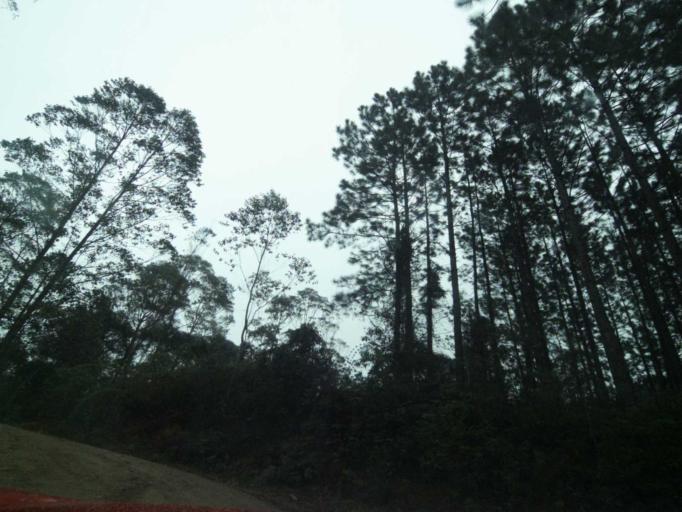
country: BR
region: Santa Catarina
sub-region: Anitapolis
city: Anitapolis
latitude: -27.9202
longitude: -49.1970
